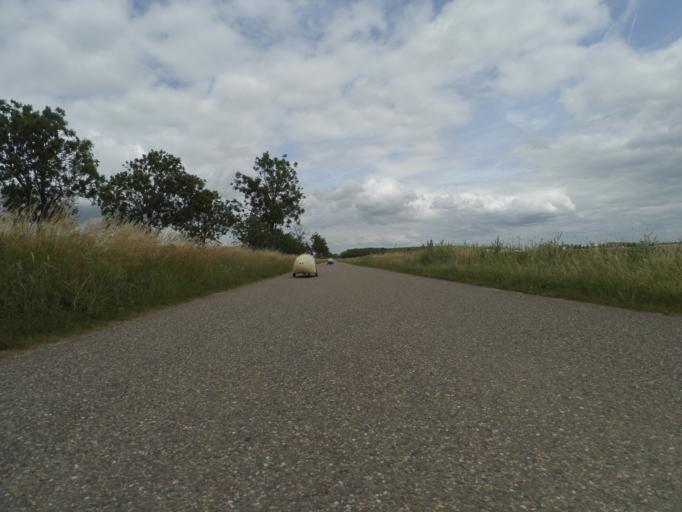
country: NL
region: North Brabant
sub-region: Gemeente Steenbergen
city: Kruisland
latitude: 51.5808
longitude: 4.4454
